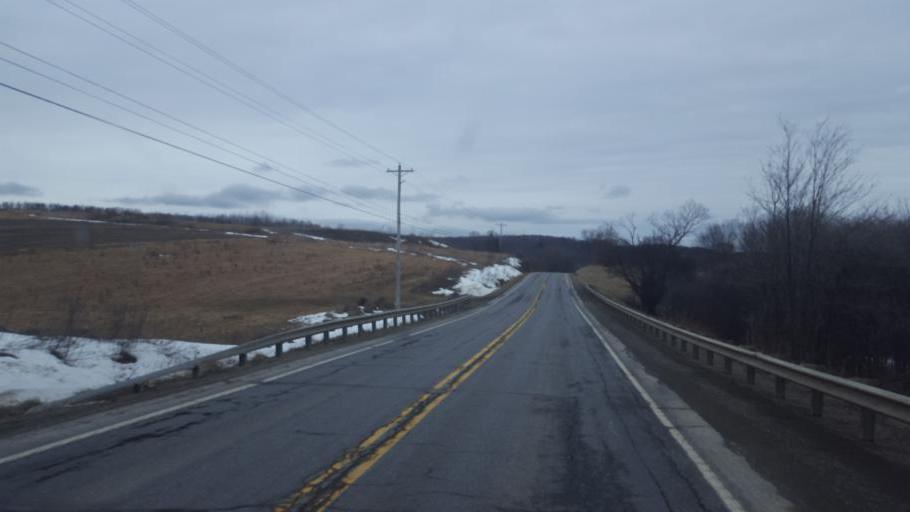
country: US
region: Pennsylvania
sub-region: Potter County
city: Coudersport
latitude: 41.8501
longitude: -77.8829
